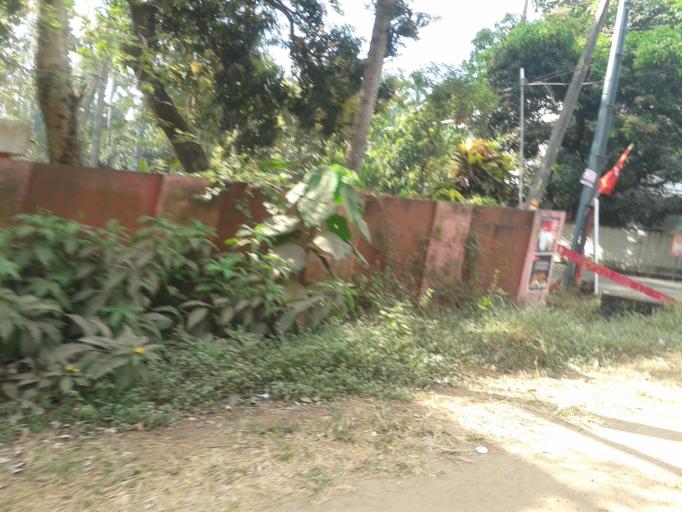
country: IN
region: Kerala
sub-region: Thrissur District
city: Kizhake Chalakudi
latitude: 10.3040
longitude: 76.3274
